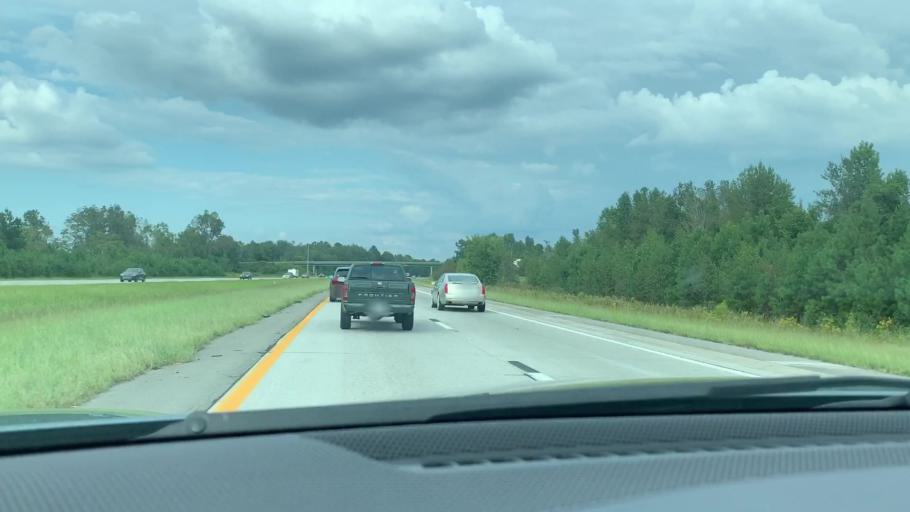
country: US
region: South Carolina
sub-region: Dorchester County
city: Saint George
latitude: 33.1271
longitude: -80.6391
